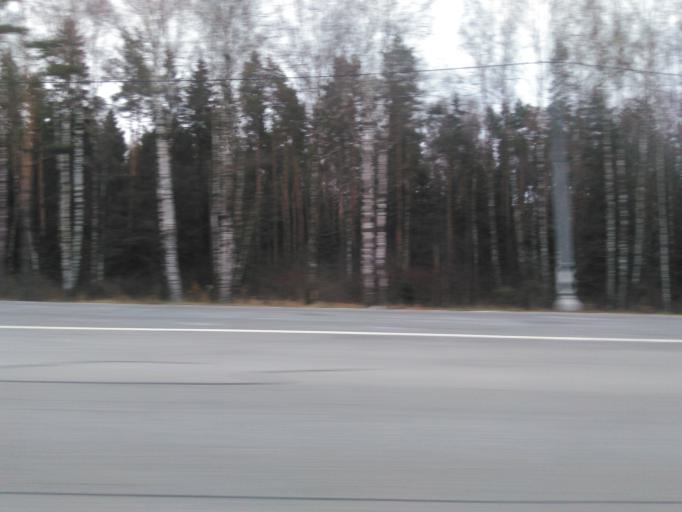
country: RU
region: Moskovskaya
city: Lesnoy
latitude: 56.0746
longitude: 37.9091
